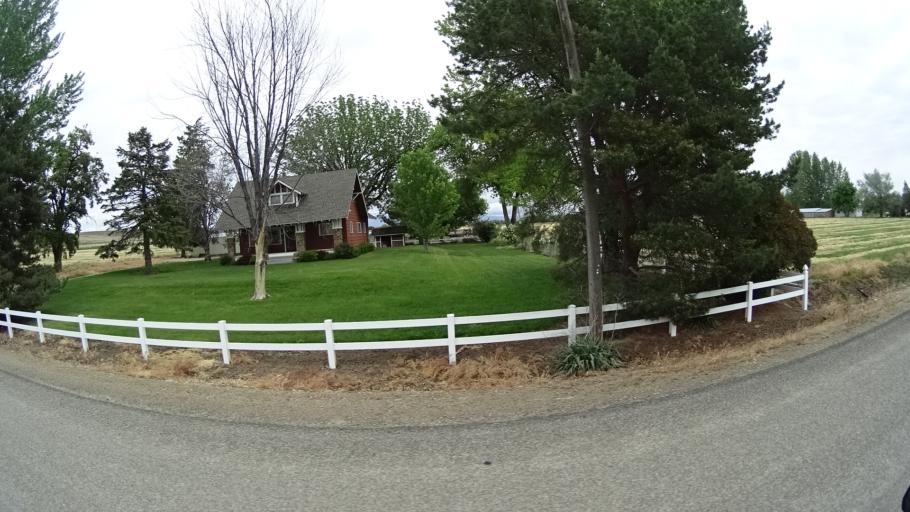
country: US
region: Idaho
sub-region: Ada County
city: Eagle
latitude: 43.7329
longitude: -116.4134
